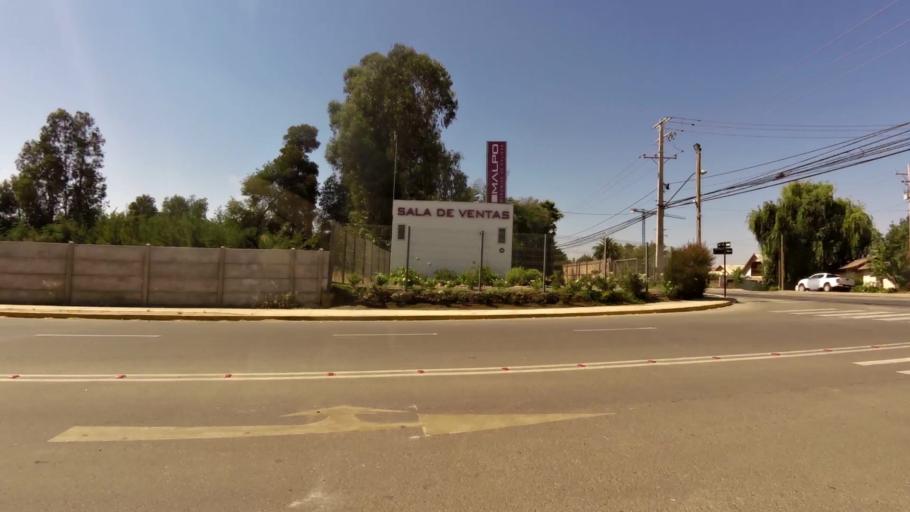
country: CL
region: Maule
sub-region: Provincia de Talca
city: Talca
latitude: -35.4312
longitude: -71.6076
